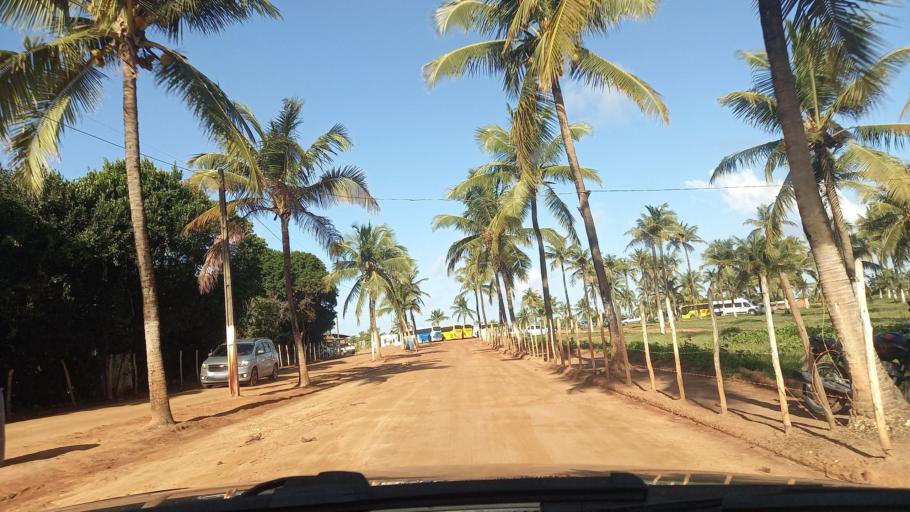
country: BR
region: Alagoas
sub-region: Marechal Deodoro
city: Marechal Deodoro
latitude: -9.8608
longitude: -35.9086
